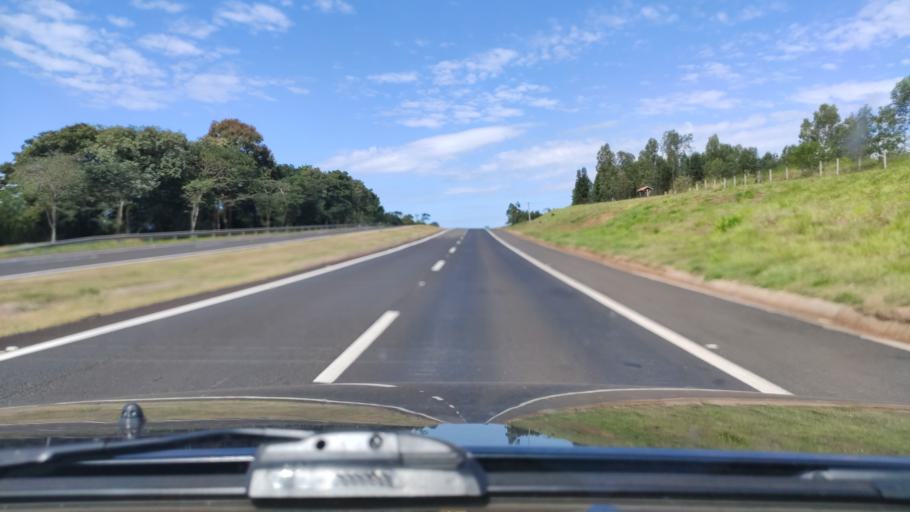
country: BR
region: Sao Paulo
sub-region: Rancharia
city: Rancharia
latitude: -22.4770
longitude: -50.9368
